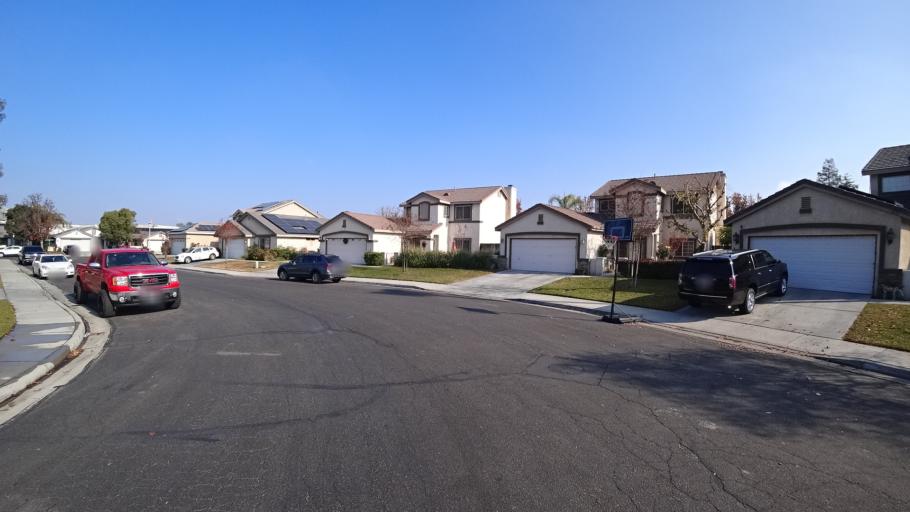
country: US
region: California
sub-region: Kern County
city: Greenacres
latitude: 35.3094
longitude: -119.0849
